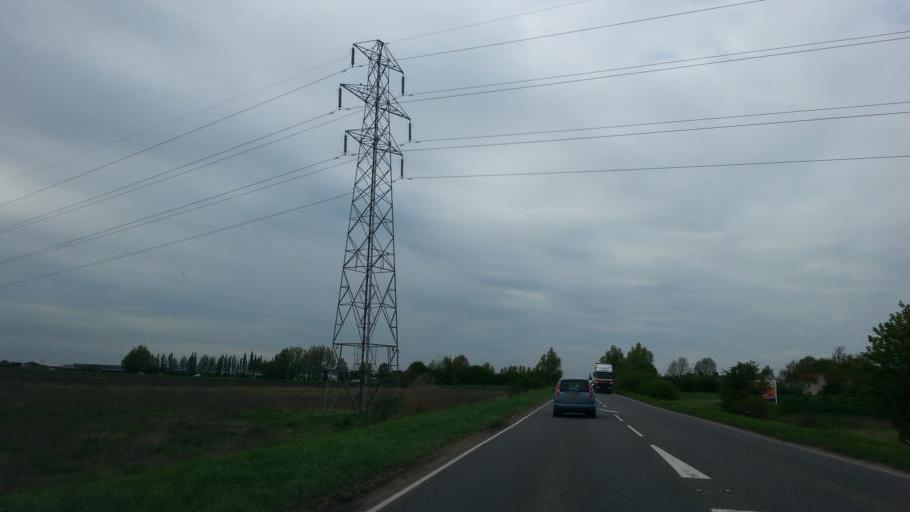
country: GB
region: England
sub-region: Cambridgeshire
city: March
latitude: 52.5505
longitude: 0.0690
